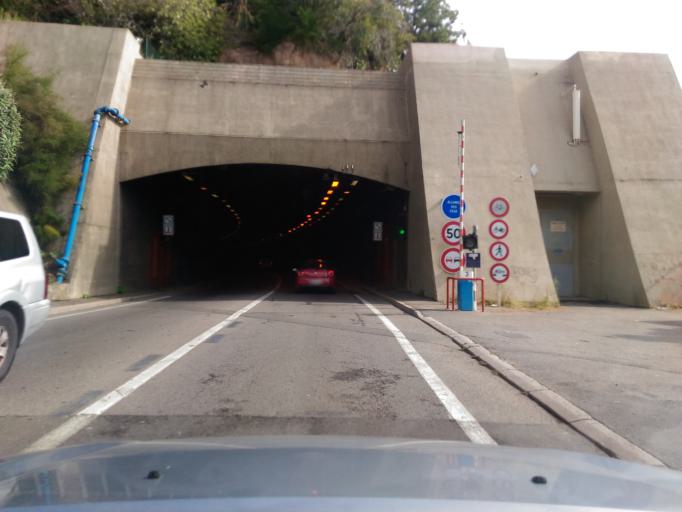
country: FR
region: Corsica
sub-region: Departement de la Haute-Corse
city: Bastia
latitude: 42.6916
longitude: 9.4506
